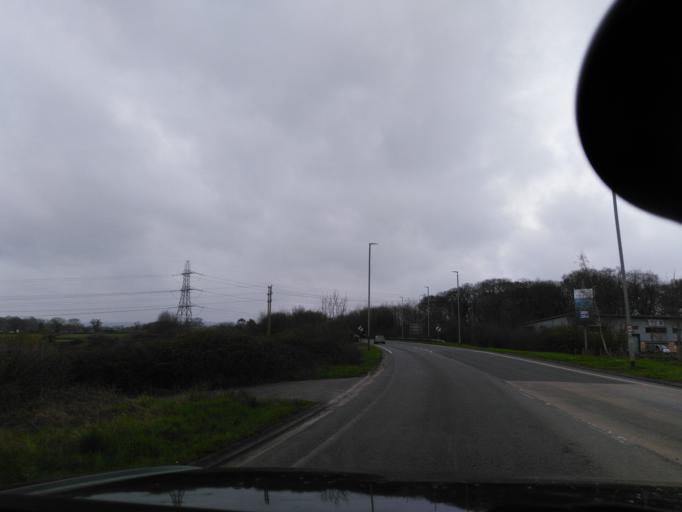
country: GB
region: England
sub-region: Somerset
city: Frome
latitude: 51.2436
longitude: -2.2900
